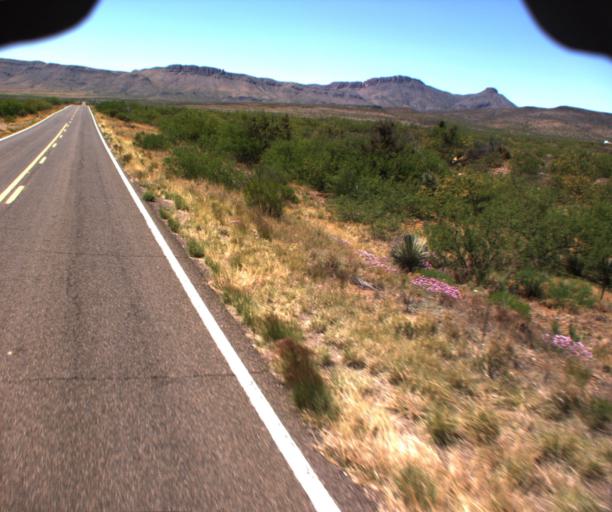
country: US
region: Arizona
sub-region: Cochise County
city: Douglas
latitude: 31.4831
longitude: -109.3472
